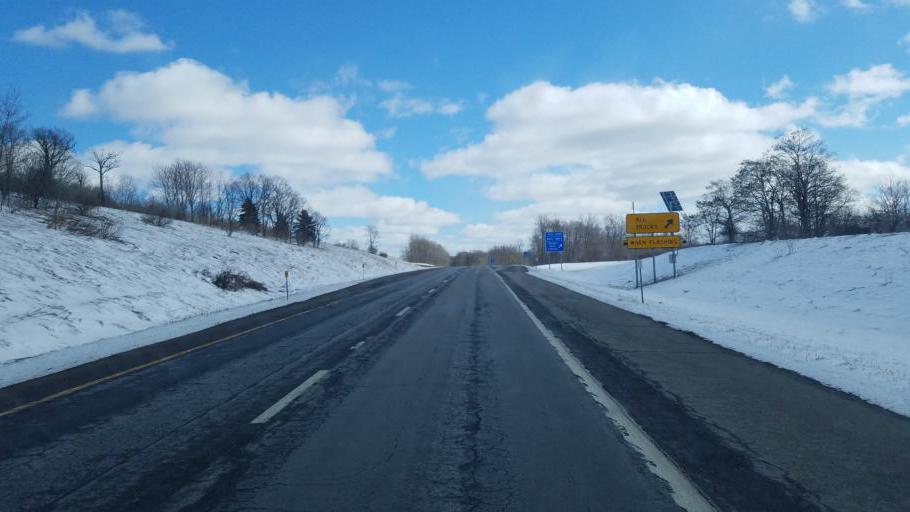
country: US
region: New York
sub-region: Chautauqua County
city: Lakewood
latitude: 42.1430
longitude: -79.3572
